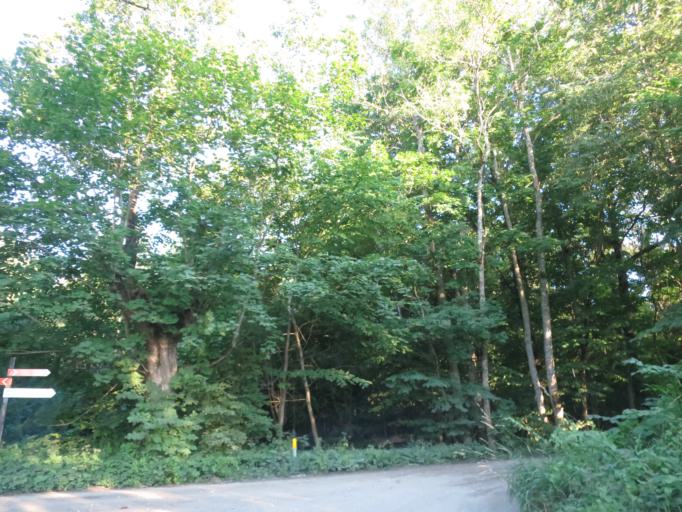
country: LV
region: Sigulda
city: Sigulda
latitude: 57.1639
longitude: 24.8263
